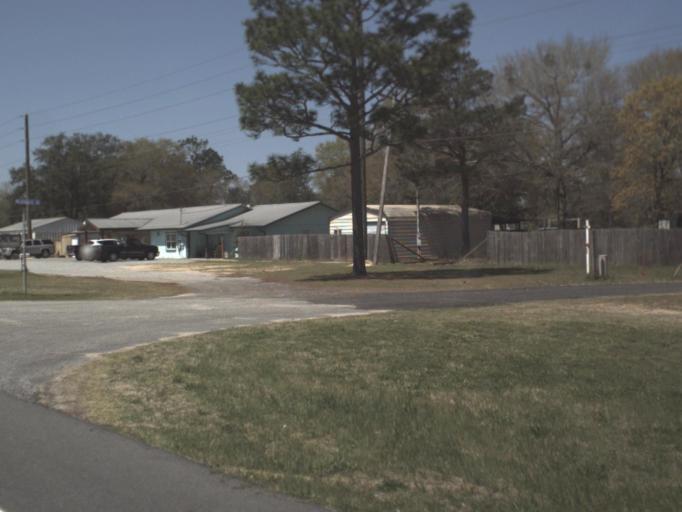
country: US
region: Florida
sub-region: Walton County
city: DeFuniak Springs
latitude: 30.7484
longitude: -86.2953
